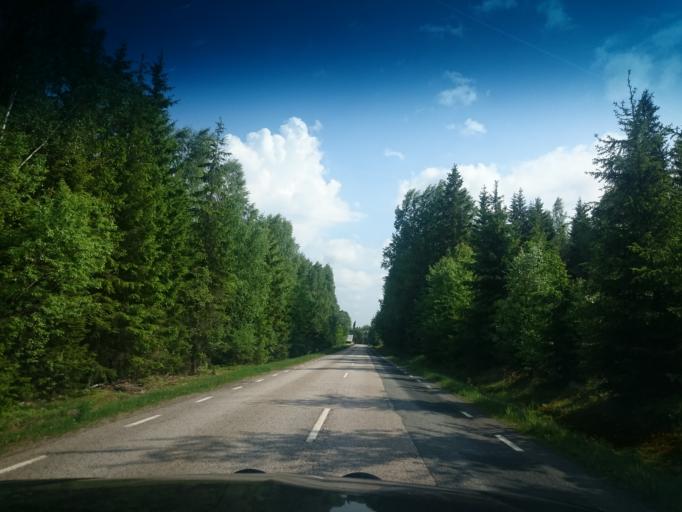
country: SE
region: Joenkoeping
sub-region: Vetlanda Kommun
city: Vetlanda
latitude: 57.3442
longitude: 15.0743
